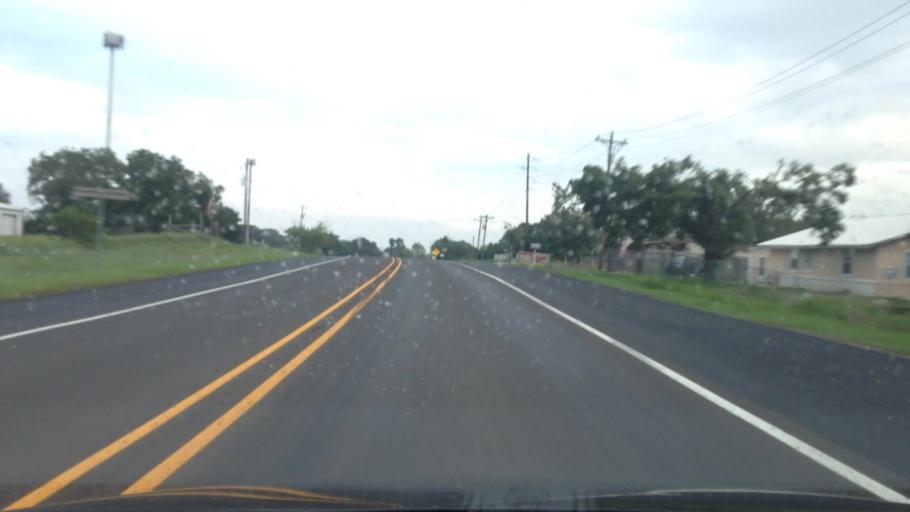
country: US
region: Texas
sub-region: Johnson County
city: Burleson
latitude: 32.4899
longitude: -97.3359
